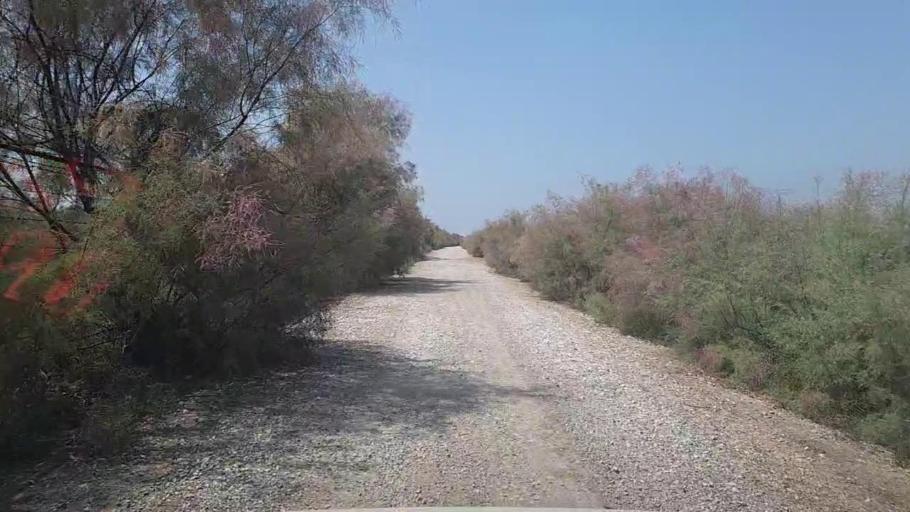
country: PK
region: Sindh
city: Kandhkot
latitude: 28.3029
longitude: 69.3545
